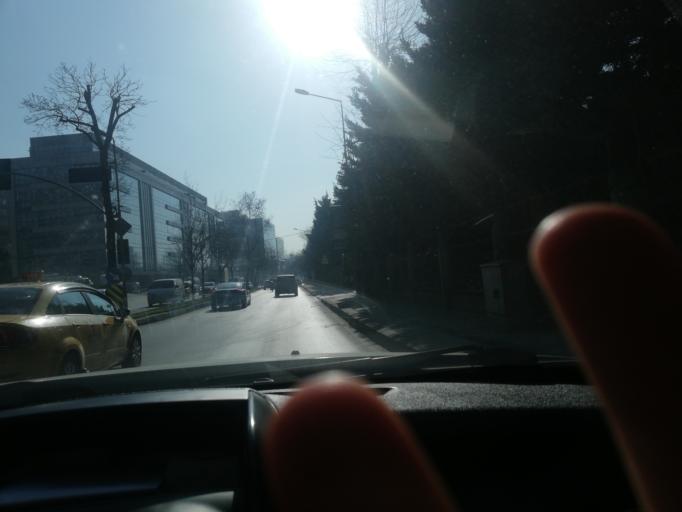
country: TR
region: Istanbul
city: Sisli
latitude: 41.0744
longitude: 28.9689
